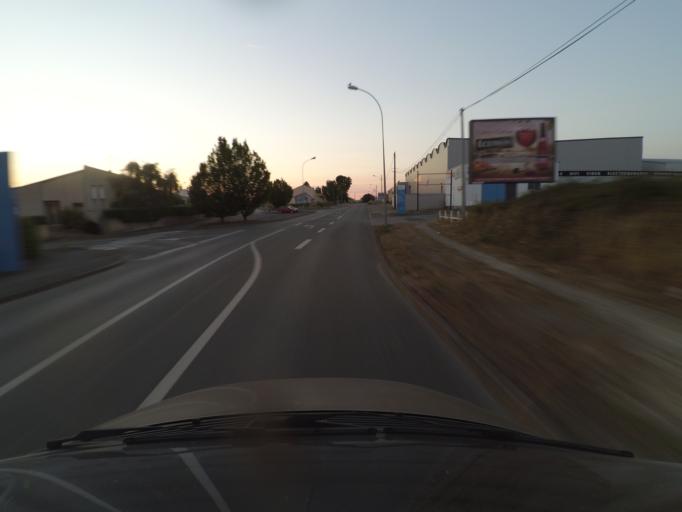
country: FR
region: Pays de la Loire
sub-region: Departement de la Vendee
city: La Roche-sur-Yon
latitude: 46.6542
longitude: -1.4455
